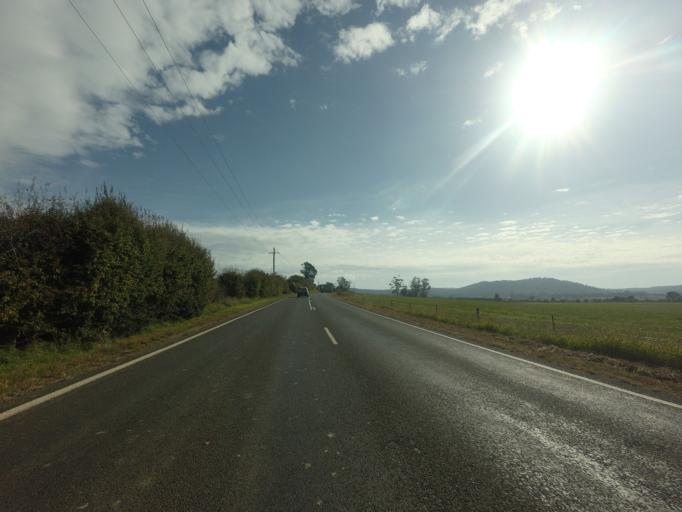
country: AU
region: Tasmania
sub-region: Meander Valley
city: Westbury
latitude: -41.5252
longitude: 146.7506
